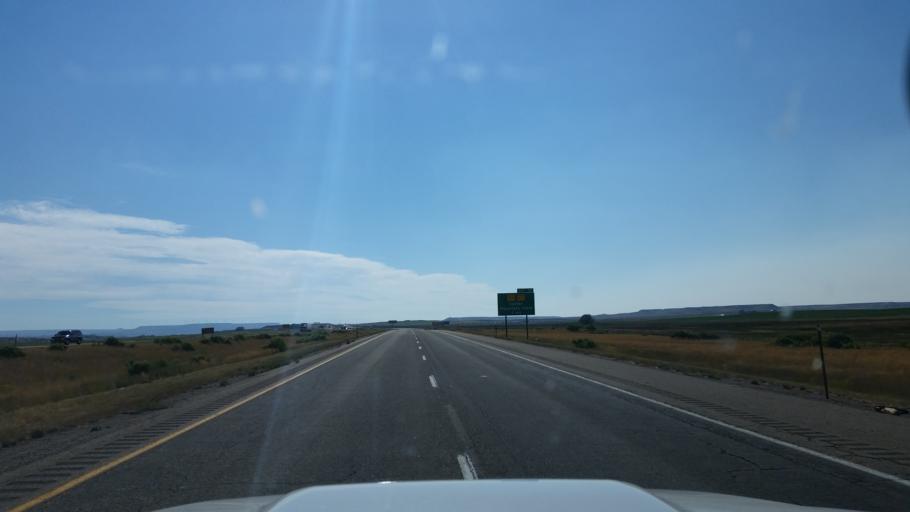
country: US
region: Wyoming
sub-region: Uinta County
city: Lyman
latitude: 41.3642
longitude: -110.3133
